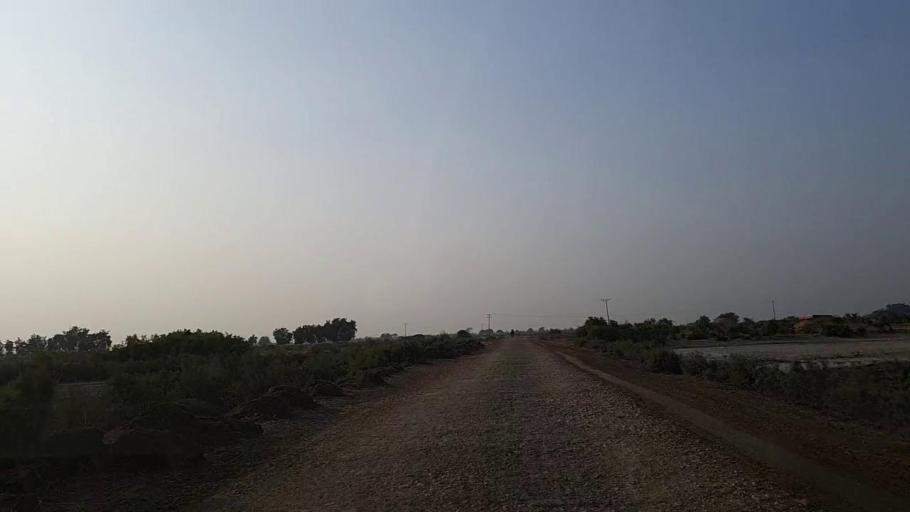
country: PK
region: Sindh
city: Thatta
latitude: 24.6931
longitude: 67.7867
